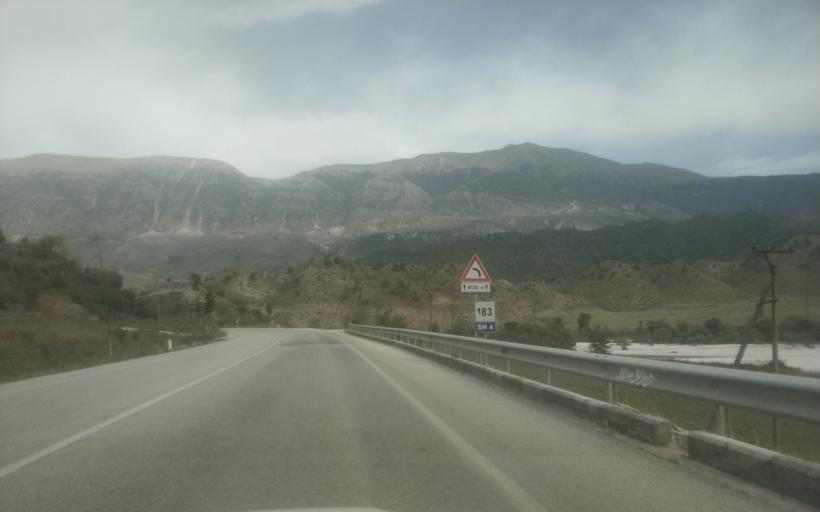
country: AL
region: Gjirokaster
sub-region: Rrethi i Gjirokastres
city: Picar
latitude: 40.2005
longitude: 20.0893
